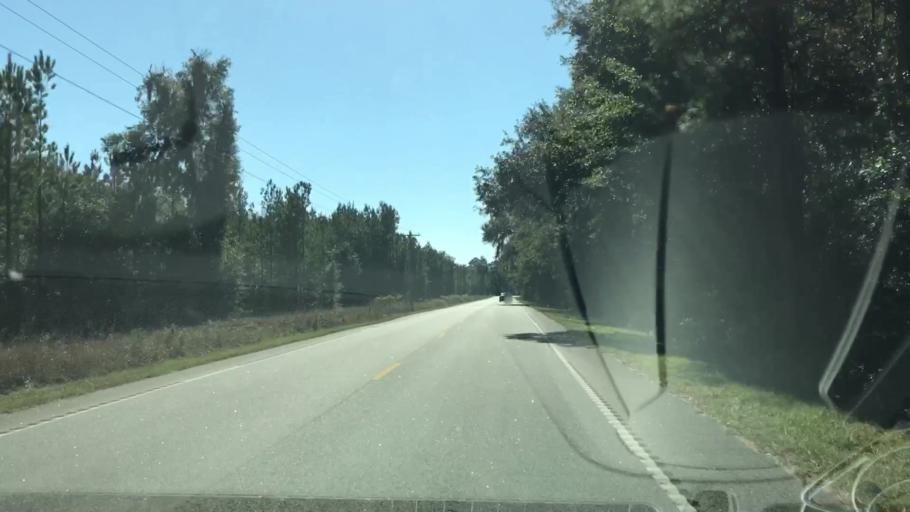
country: US
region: South Carolina
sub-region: Jasper County
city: Ridgeland
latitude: 32.5007
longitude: -80.8860
